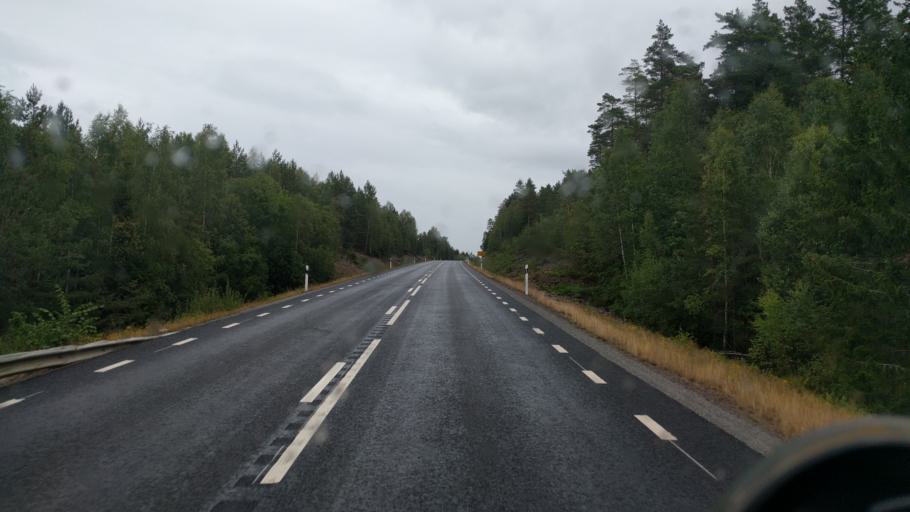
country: SE
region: Kalmar
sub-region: Vasterviks Kommun
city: Ankarsrum
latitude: 57.7123
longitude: 16.3368
